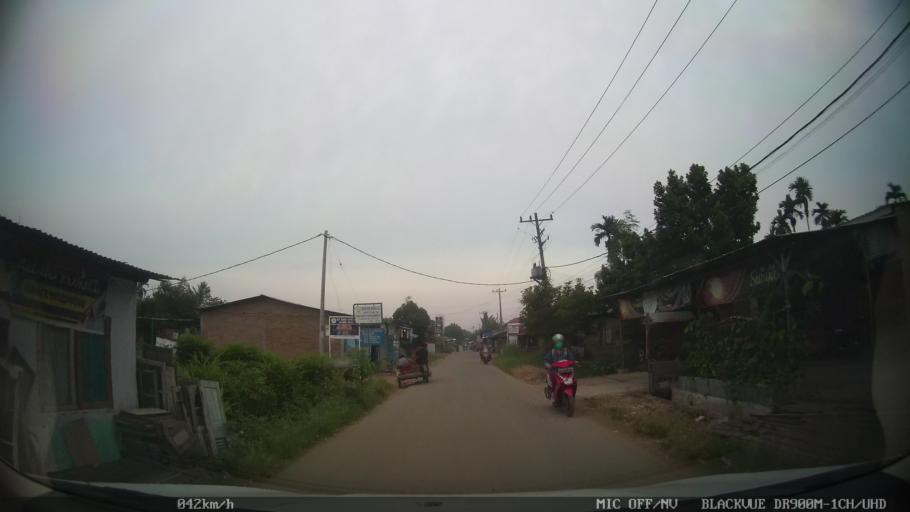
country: ID
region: North Sumatra
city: Deli Tua
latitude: 3.5486
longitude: 98.7281
